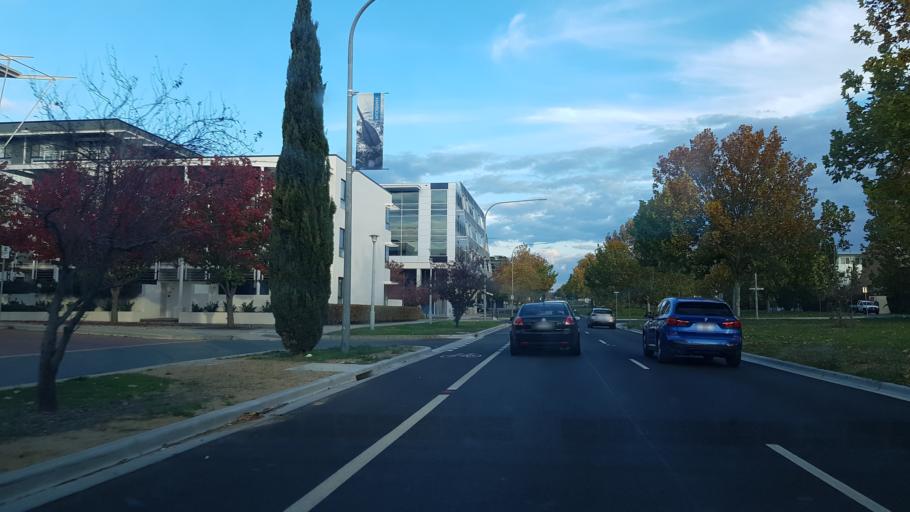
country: AU
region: Australian Capital Territory
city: Forrest
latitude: -35.3159
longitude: 149.1455
